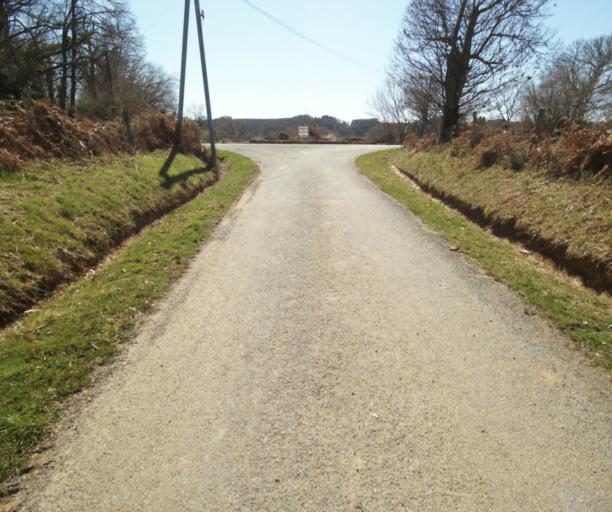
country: FR
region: Limousin
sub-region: Departement de la Correze
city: Uzerche
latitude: 45.3979
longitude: 1.6290
